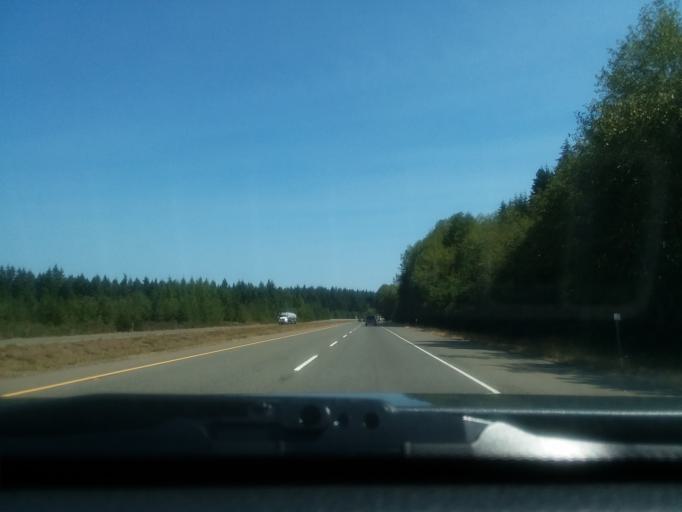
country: CA
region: British Columbia
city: Port Alberni
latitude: 49.4205
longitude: -124.7135
